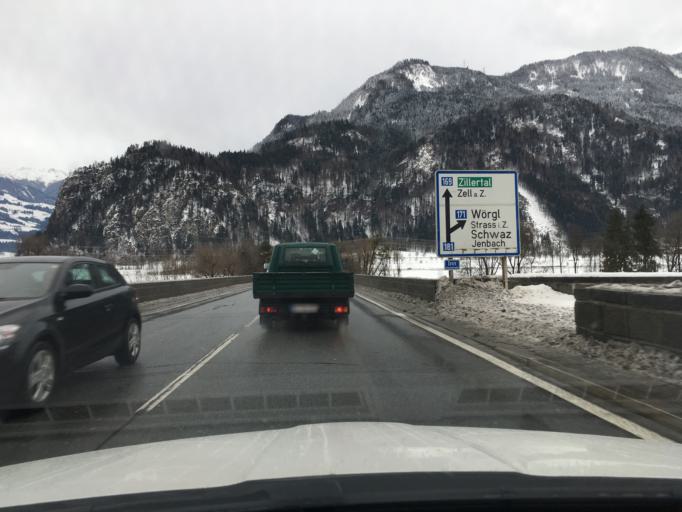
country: AT
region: Tyrol
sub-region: Politischer Bezirk Schwaz
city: Wiesing
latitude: 47.4012
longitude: 11.8039
